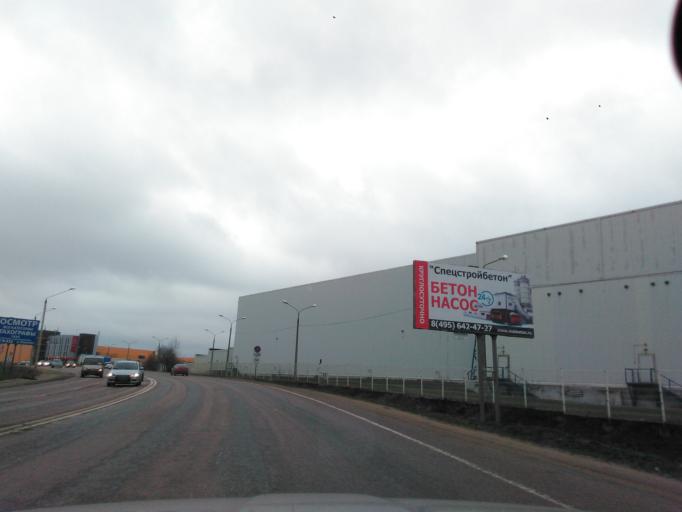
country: RU
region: Moskovskaya
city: Pavlovskaya Sloboda
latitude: 55.8136
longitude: 37.1126
